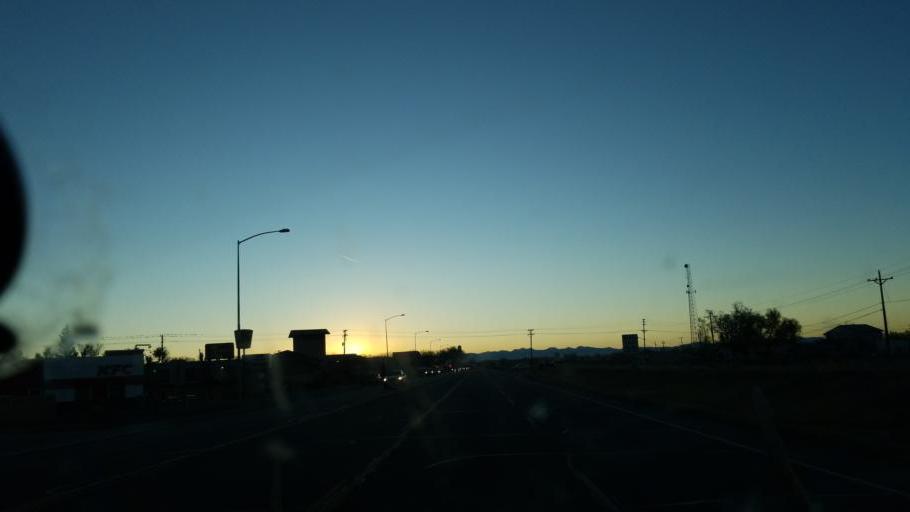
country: US
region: Colorado
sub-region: Alamosa County
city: Alamosa
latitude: 37.4718
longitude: -105.8866
